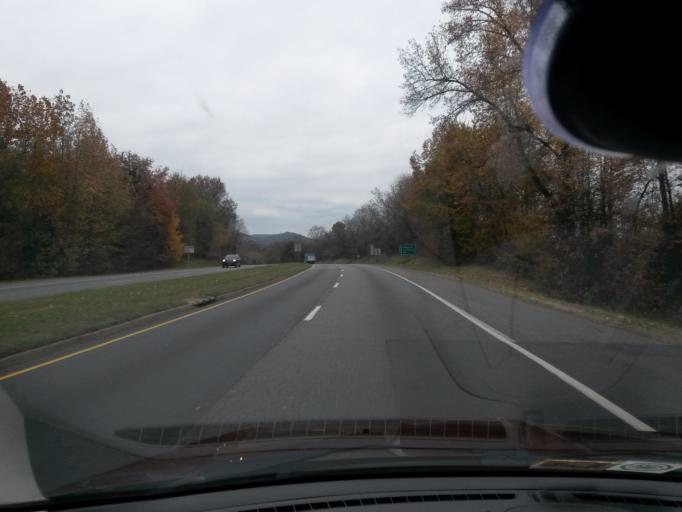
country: US
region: Virginia
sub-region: City of Charlottesville
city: Charlottesville
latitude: 38.0543
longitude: -78.5200
